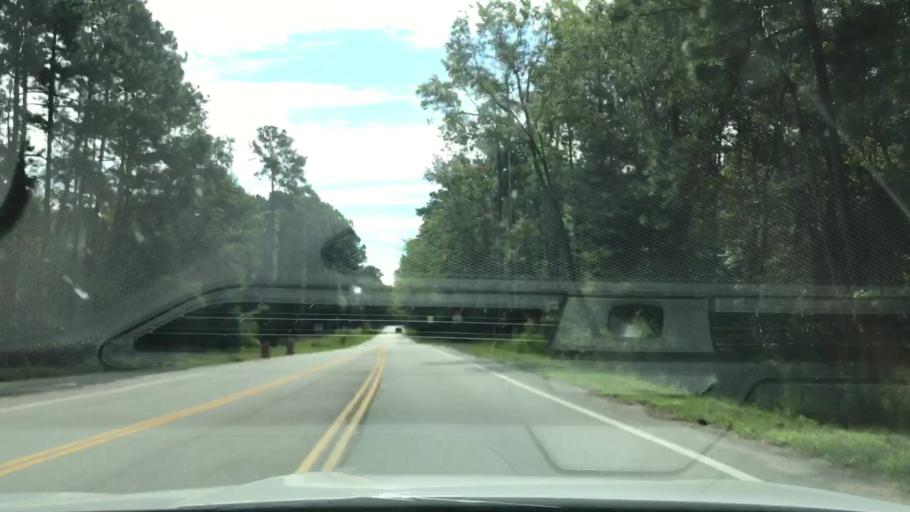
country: US
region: South Carolina
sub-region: Dorchester County
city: Centerville
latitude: 32.9467
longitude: -80.2016
